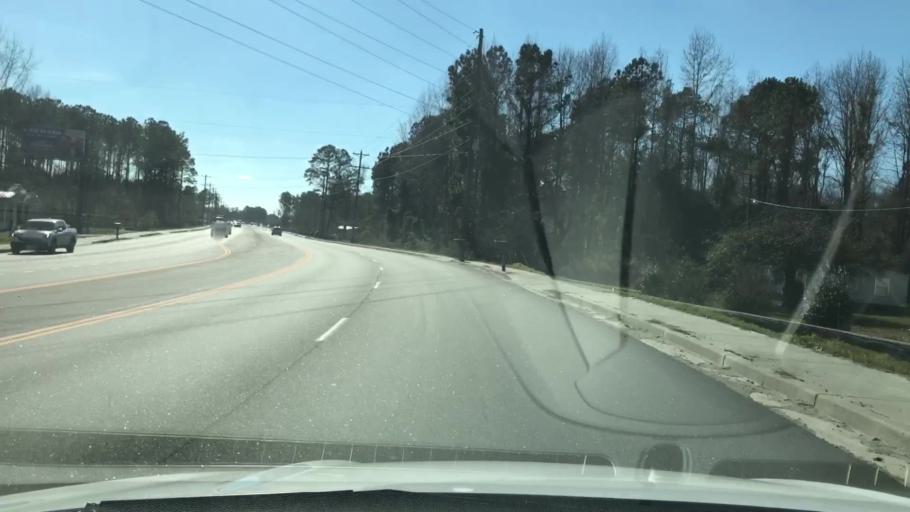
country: US
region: South Carolina
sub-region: Horry County
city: Garden City
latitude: 33.6380
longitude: -79.0327
